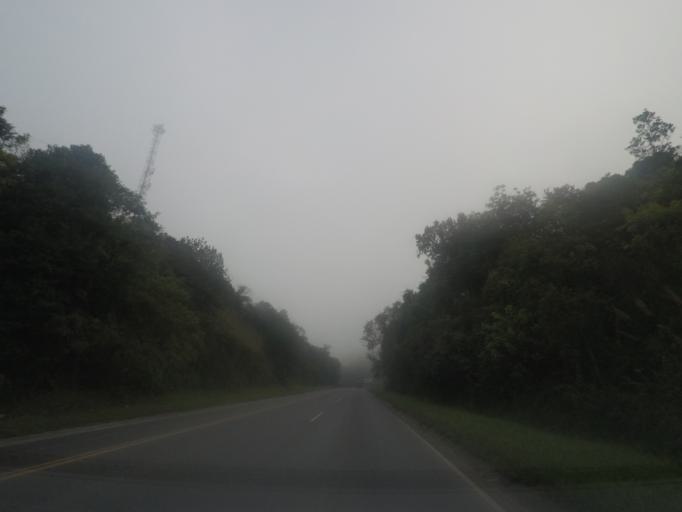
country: BR
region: Parana
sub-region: Almirante Tamandare
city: Almirante Tamandare
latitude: -25.2807
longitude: -49.3038
